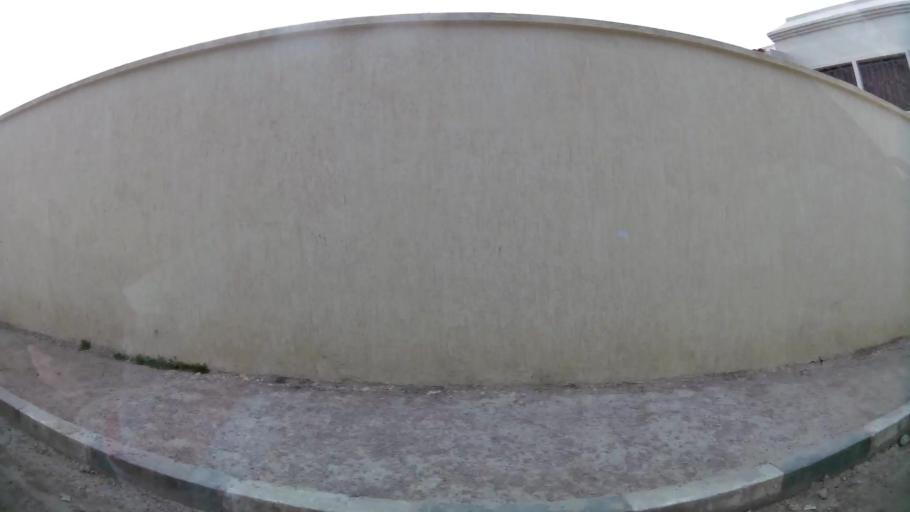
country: MA
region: Tanger-Tetouan
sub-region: Tanger-Assilah
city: Boukhalef
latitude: 35.7075
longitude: -5.9002
